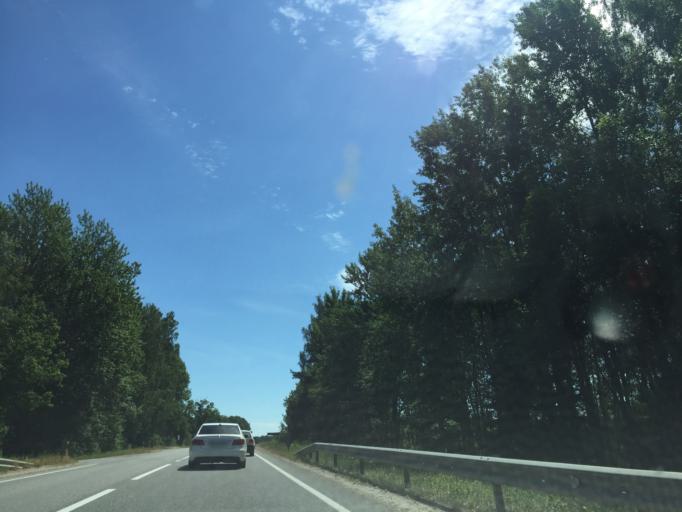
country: LV
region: Broceni
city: Broceni
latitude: 56.6586
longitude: 22.6208
